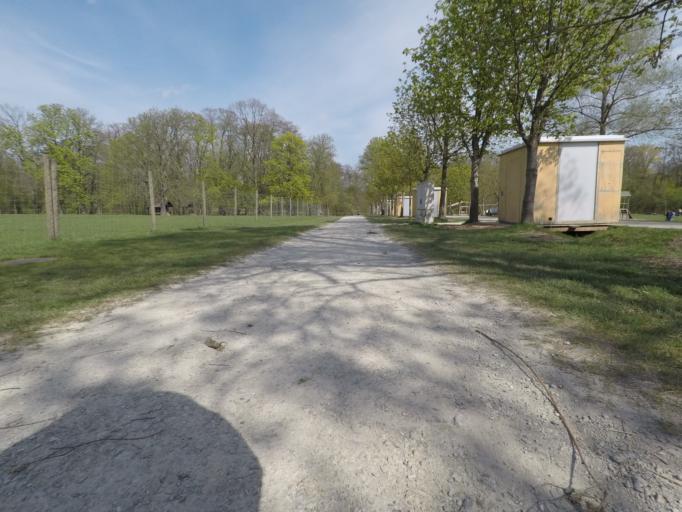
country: AT
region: Lower Austria
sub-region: Politischer Bezirk Modling
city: Perchtoldsdorf
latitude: 48.1671
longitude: 16.2535
